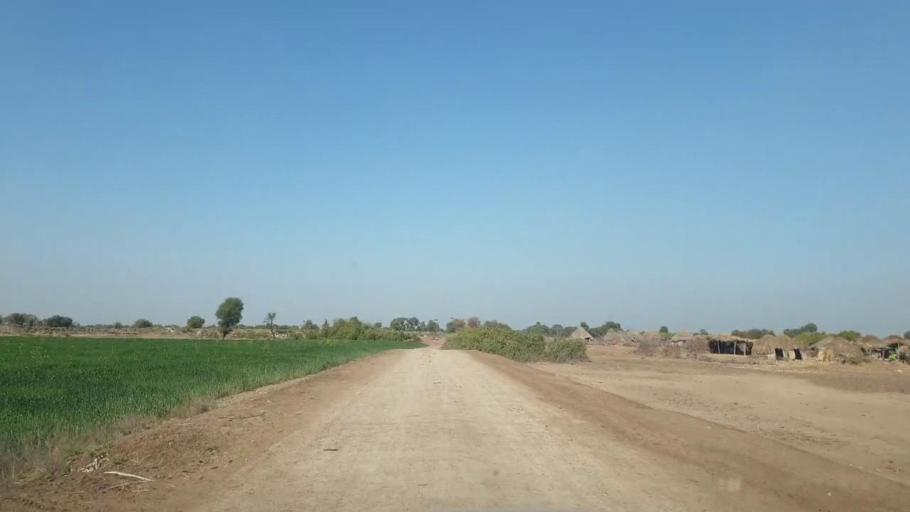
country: PK
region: Sindh
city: Tando Adam
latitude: 25.6475
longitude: 68.6863
